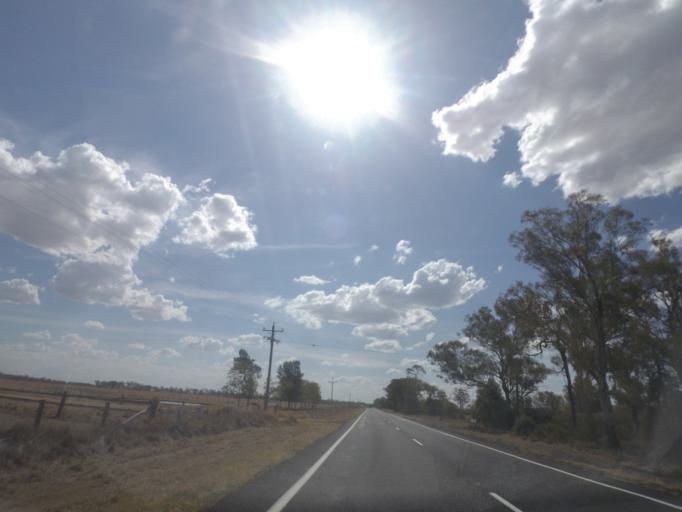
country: AU
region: New South Wales
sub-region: Moree Plains
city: Boggabilla
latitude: -28.4121
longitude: 151.1068
